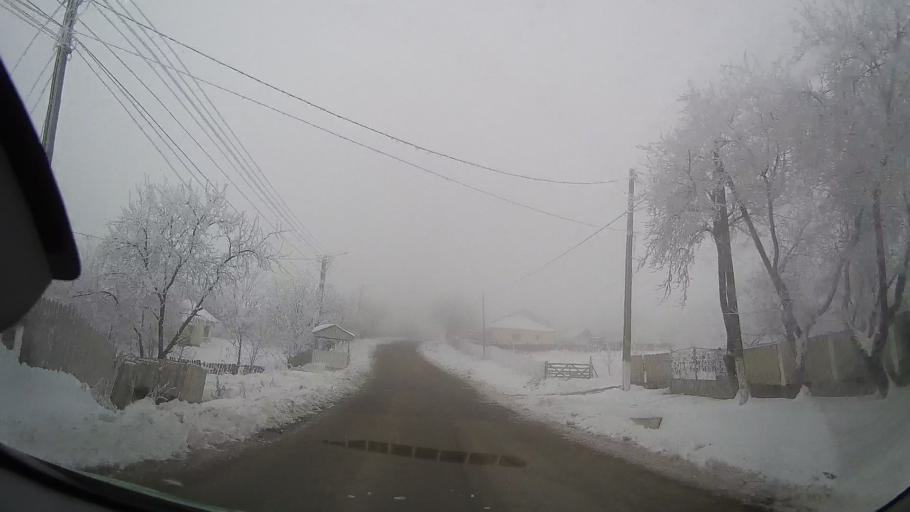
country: RO
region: Iasi
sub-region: Comuna Tansa
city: Suhulet
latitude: 46.8997
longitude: 27.2541
